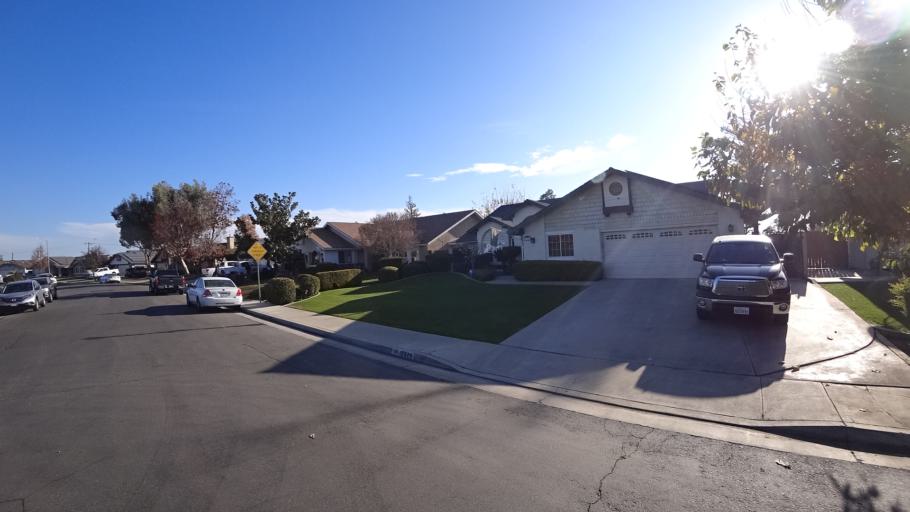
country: US
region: California
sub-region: Kern County
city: Rosedale
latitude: 35.3481
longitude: -119.1468
